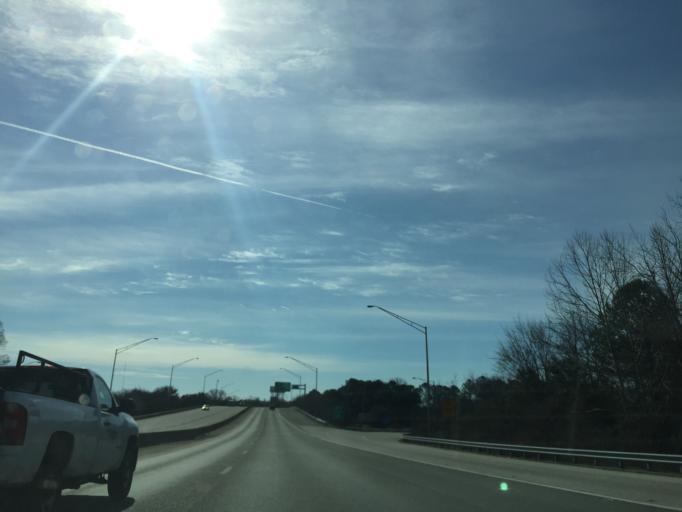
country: US
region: Virginia
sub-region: City of Hampton
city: East Hampton
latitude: 37.0261
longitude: -76.3315
